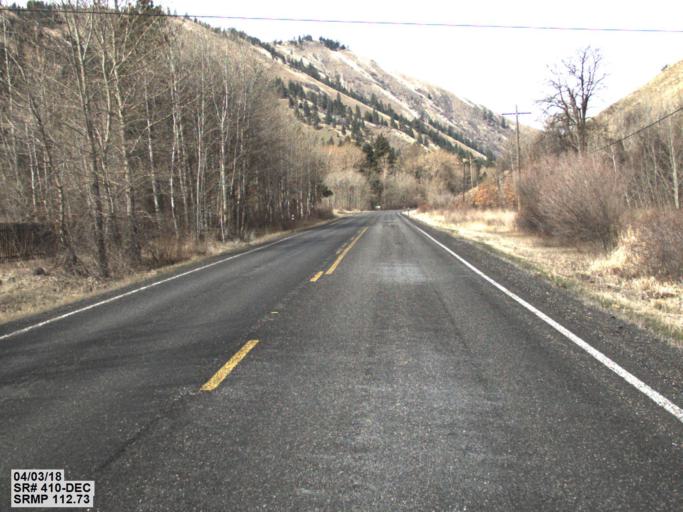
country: US
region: Washington
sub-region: Yakima County
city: Tieton
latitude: 46.7714
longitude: -120.8480
